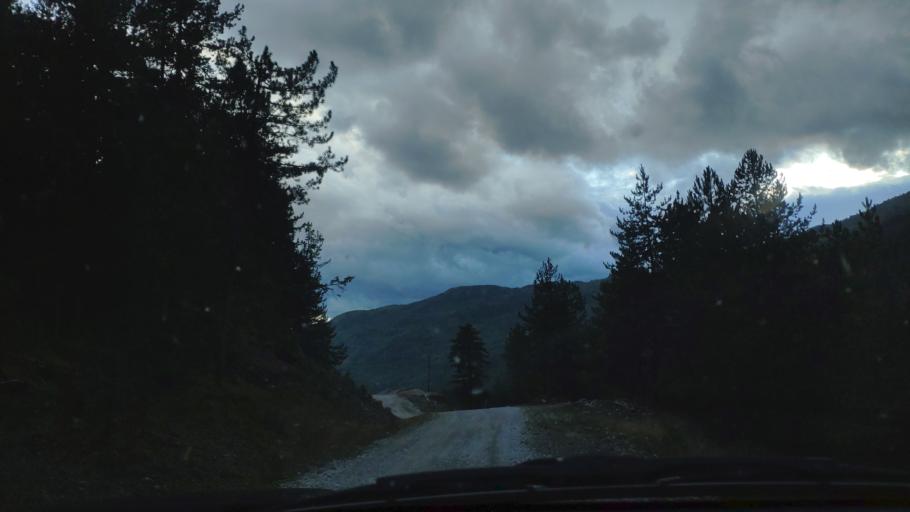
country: AL
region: Korce
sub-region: Rrethi i Kolonjes
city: Erseke
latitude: 40.2859
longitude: 20.8622
